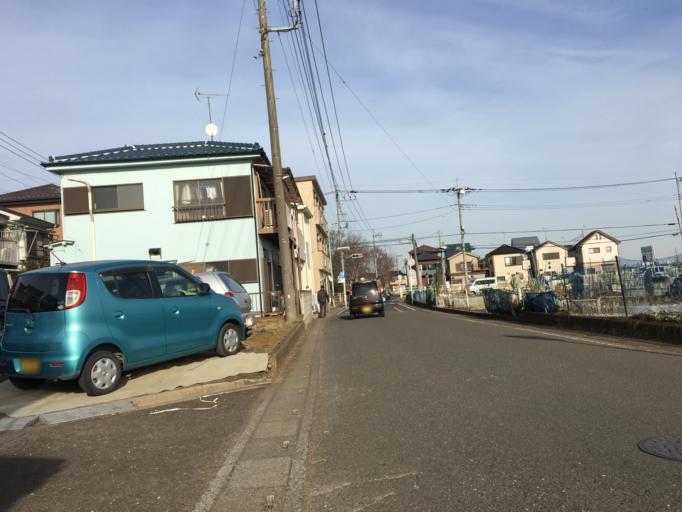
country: JP
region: Saitama
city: Oi
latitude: 35.8350
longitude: 139.5340
